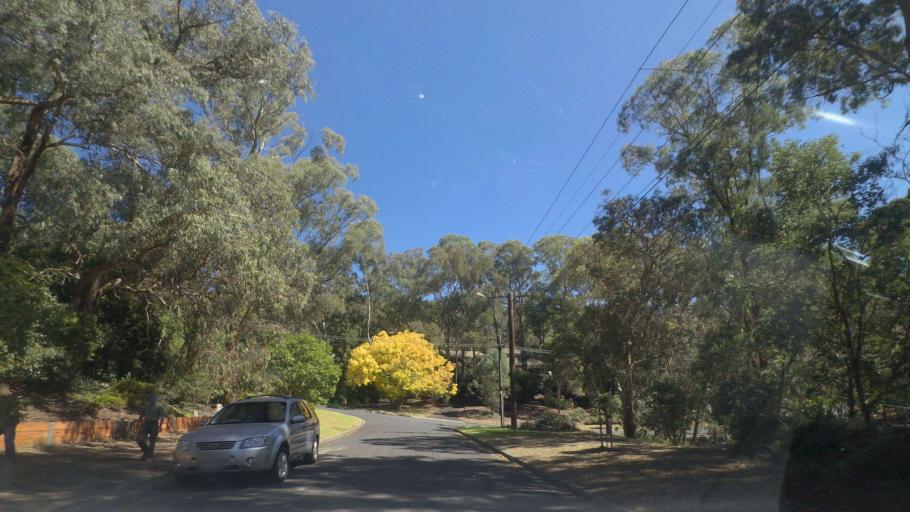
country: AU
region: Victoria
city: Mitcham
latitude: -37.7951
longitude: 145.2005
